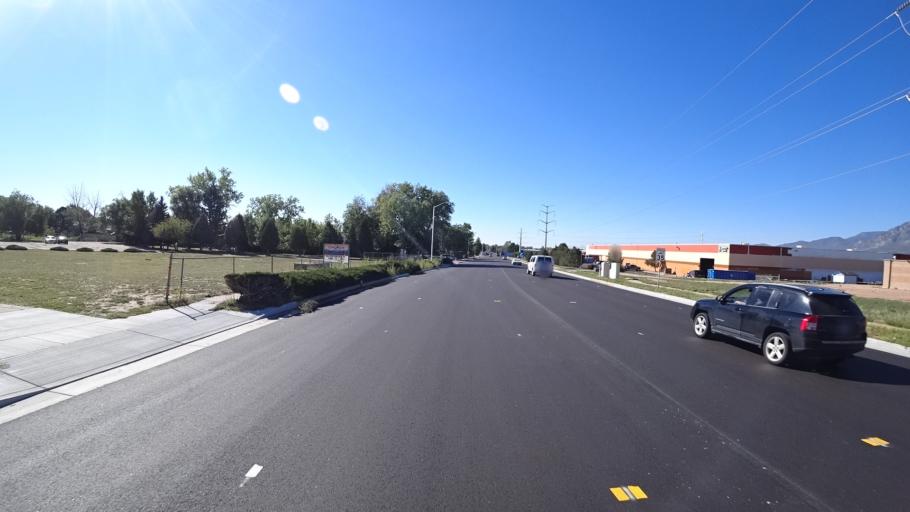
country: US
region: Colorado
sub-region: El Paso County
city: Stratmoor
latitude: 38.7920
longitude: -104.7541
